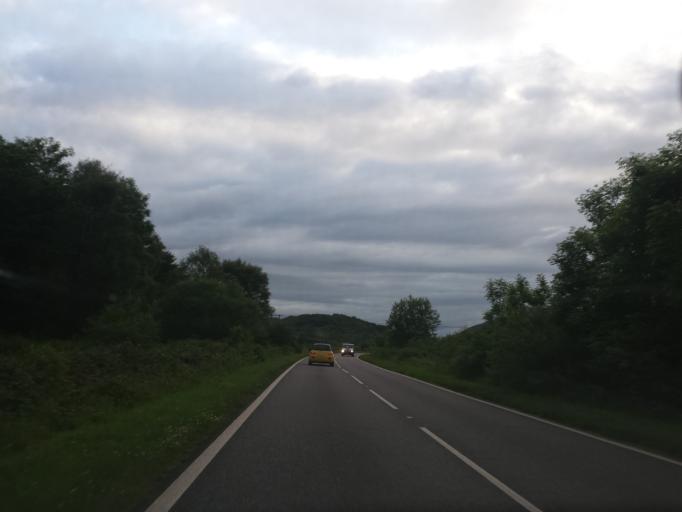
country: GB
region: Scotland
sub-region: Highland
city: Fort William
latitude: 57.2854
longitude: -5.5413
